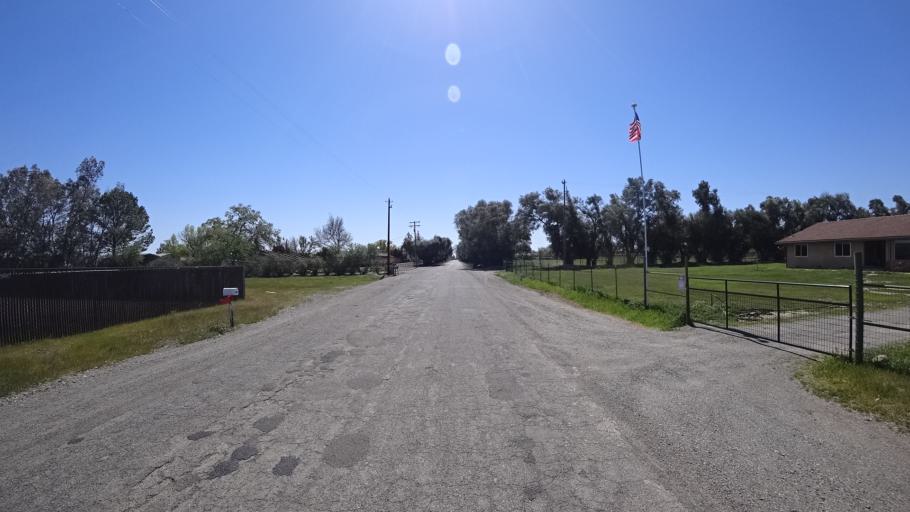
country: US
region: California
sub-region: Glenn County
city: Orland
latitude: 39.7738
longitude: -122.2386
